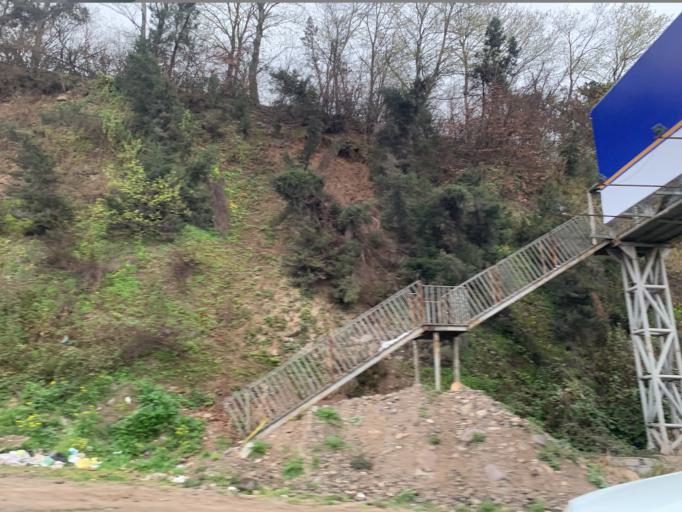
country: IR
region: Mazandaran
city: Amol
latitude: 36.3931
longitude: 52.3485
